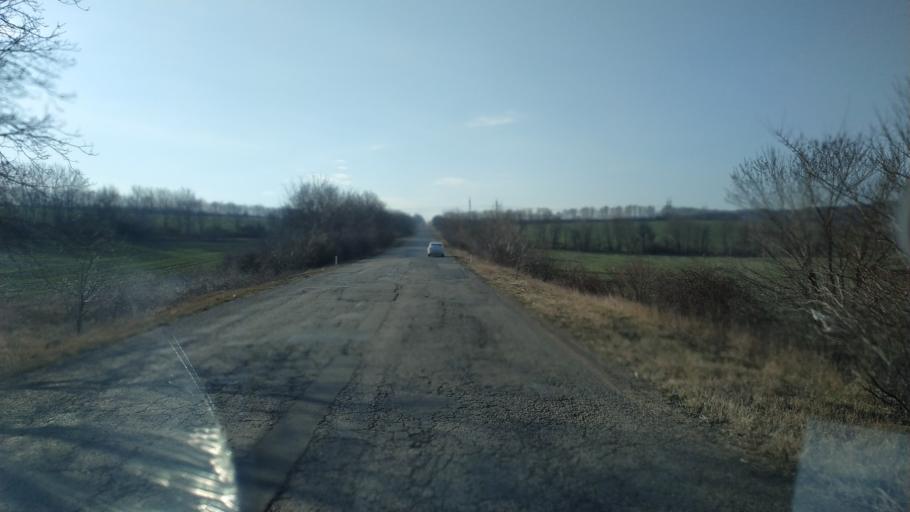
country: MD
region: Chisinau
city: Singera
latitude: 46.8793
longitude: 29.0394
